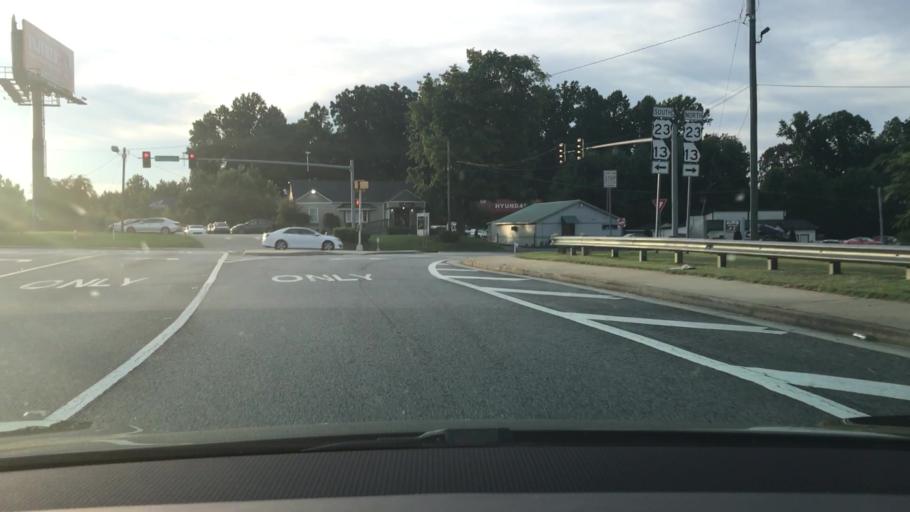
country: US
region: Georgia
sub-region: Gwinnett County
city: Duluth
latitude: 33.9823
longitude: -84.1553
